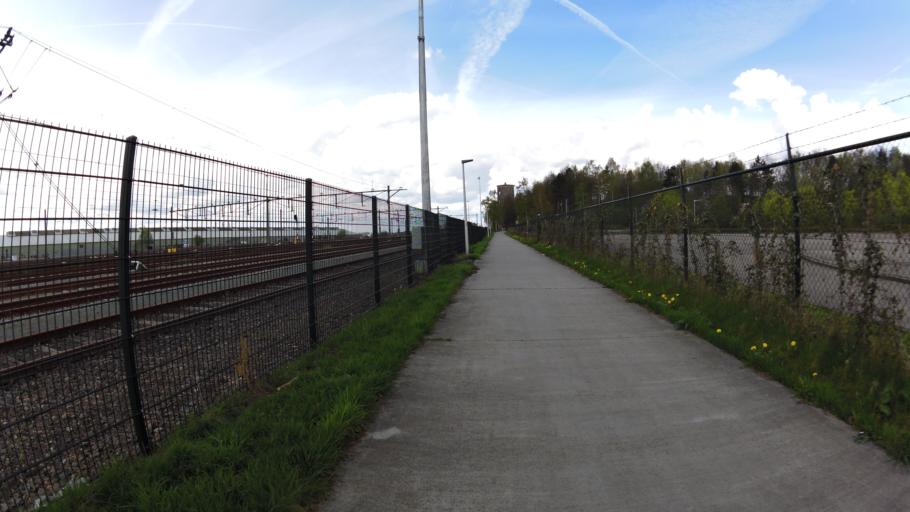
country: NL
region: Limburg
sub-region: Gemeente Heerlen
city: Heerlen
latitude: 50.8939
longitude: 5.9645
